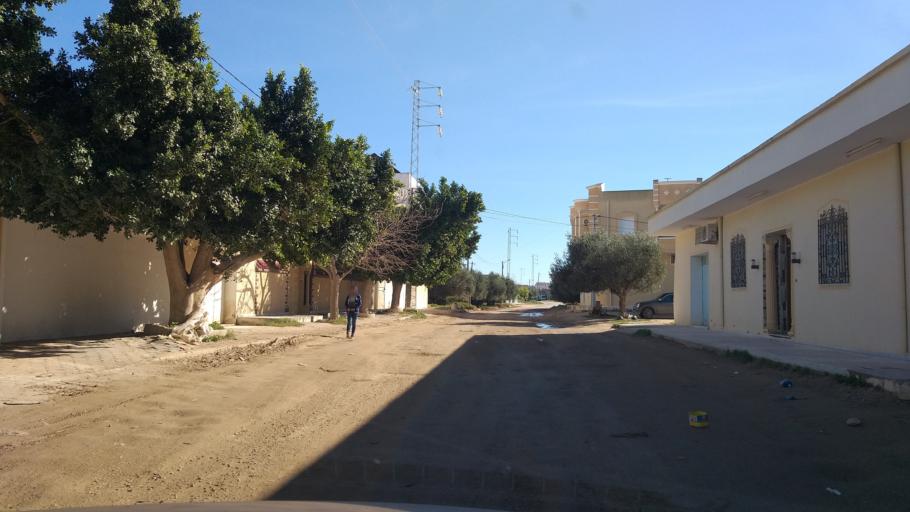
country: TN
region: Al Mahdiyah
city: El Jem
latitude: 35.2929
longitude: 10.7168
